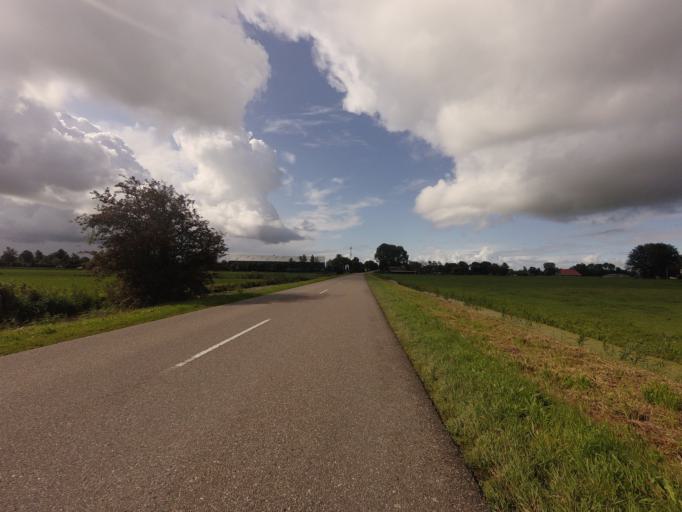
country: NL
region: Friesland
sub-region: Gemeente Boarnsterhim
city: Warten
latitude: 53.1528
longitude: 5.9077
